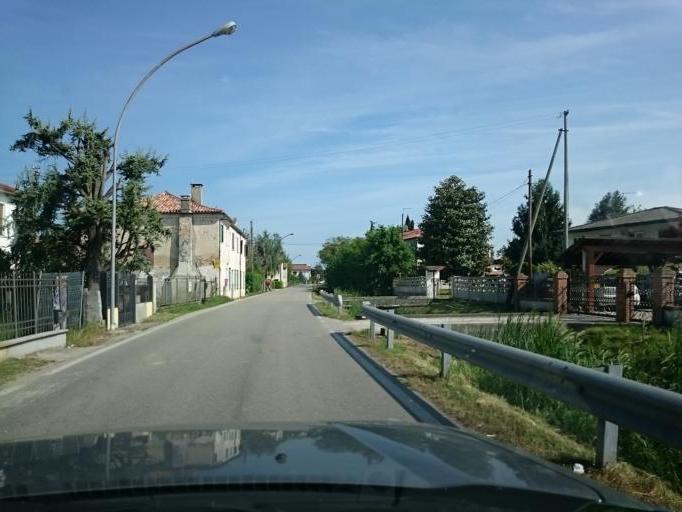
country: IT
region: Veneto
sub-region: Provincia di Venezia
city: Mira Taglio
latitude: 45.4198
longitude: 12.1398
